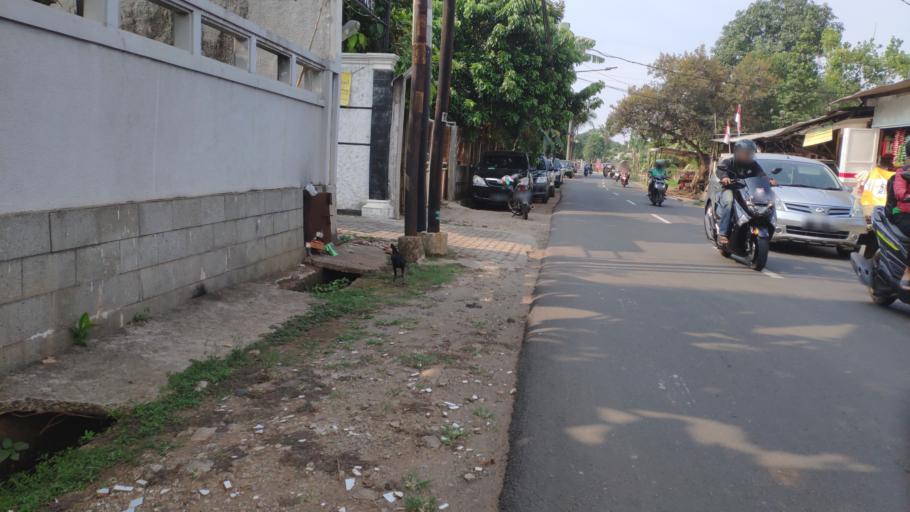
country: ID
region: West Java
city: Depok
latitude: -6.3217
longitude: 106.8142
